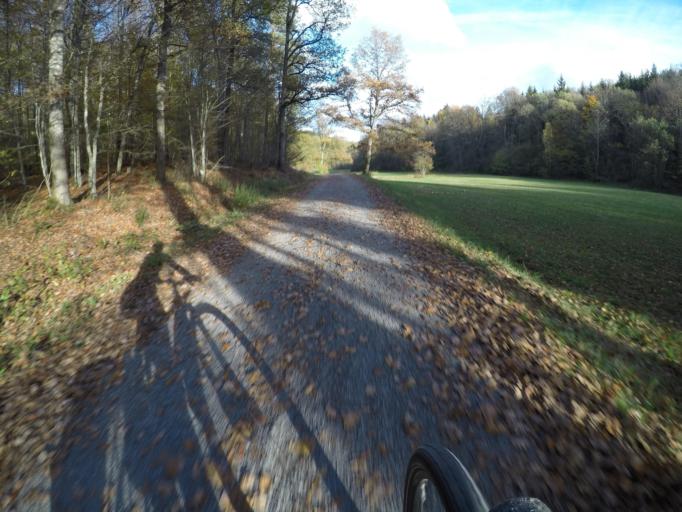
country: DE
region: Baden-Wuerttemberg
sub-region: Regierungsbezirk Stuttgart
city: Steinenbronn
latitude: 48.7011
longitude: 9.0890
